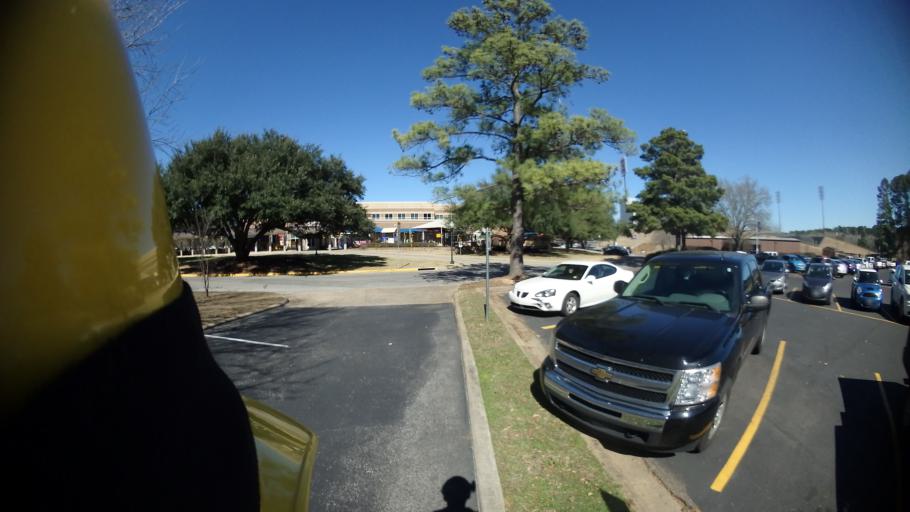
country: US
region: Texas
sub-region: Nacogdoches County
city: Nacogdoches
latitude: 31.6244
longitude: -94.6464
